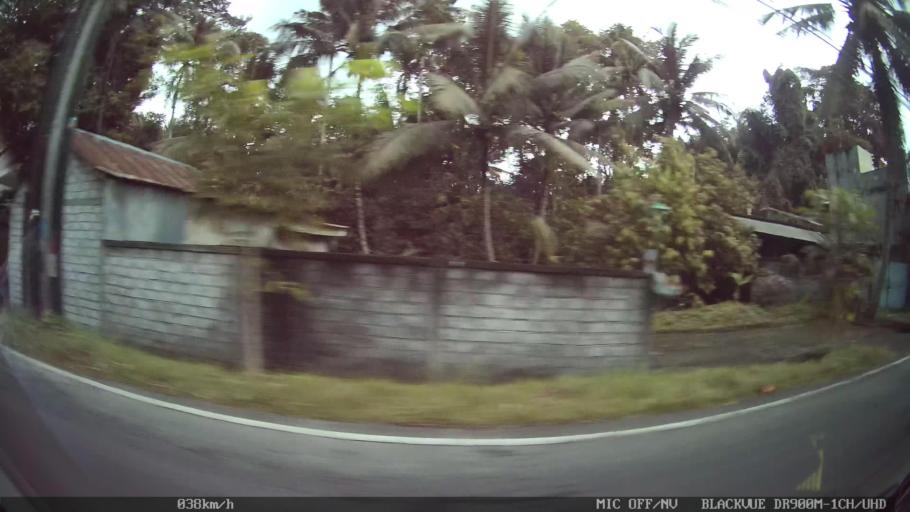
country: ID
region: Bali
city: Banjar Sempidi
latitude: -8.5219
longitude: 115.1921
